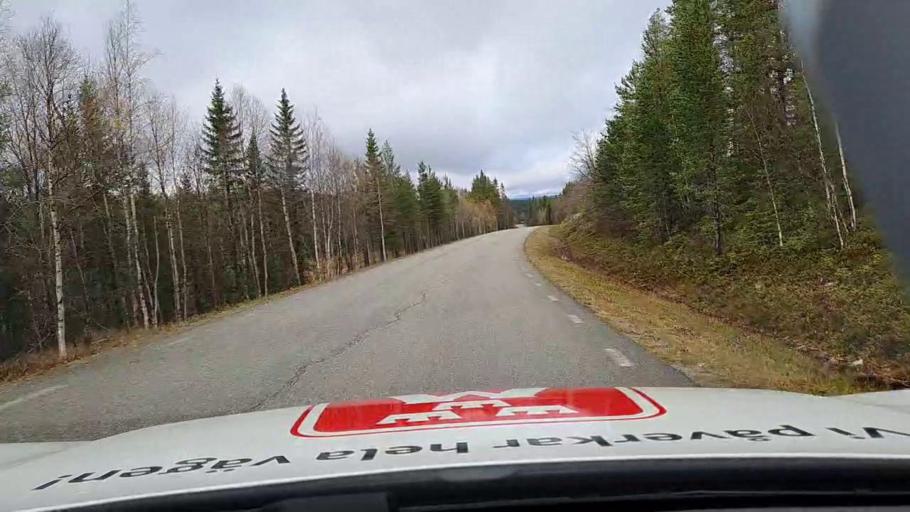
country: SE
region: Jaemtland
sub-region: Bergs Kommun
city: Hoverberg
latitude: 63.0379
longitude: 14.0185
